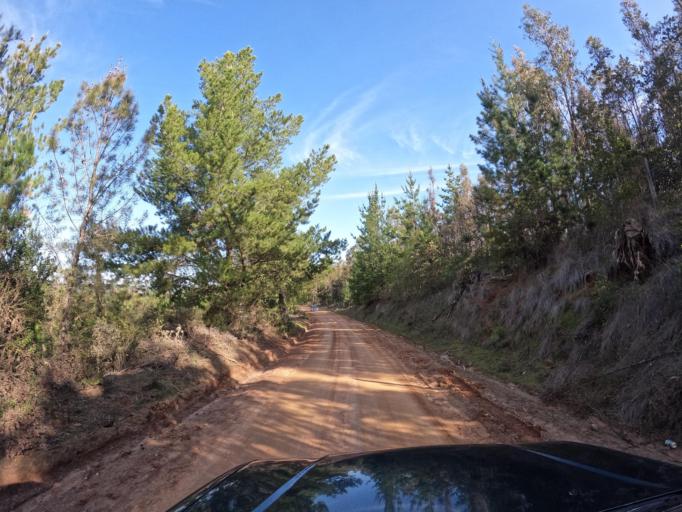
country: CL
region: Biobio
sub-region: Provincia de Biobio
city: La Laja
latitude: -37.1191
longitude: -72.7381
